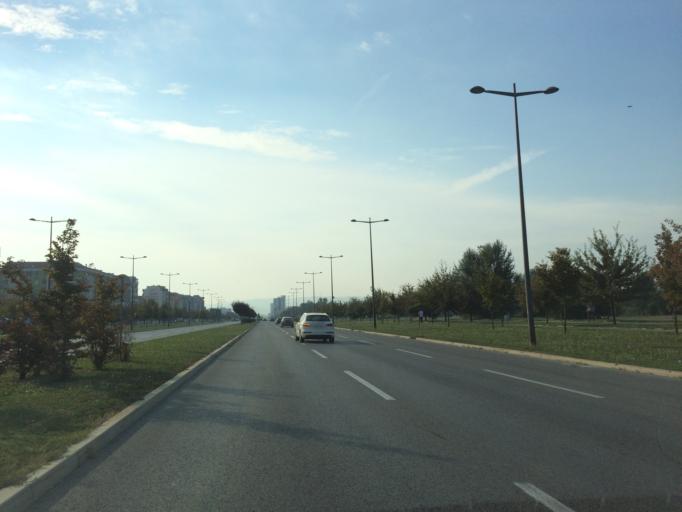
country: RS
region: Autonomna Pokrajina Vojvodina
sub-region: Juznobacki Okrug
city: Novi Sad
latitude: 45.2585
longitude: 19.8097
